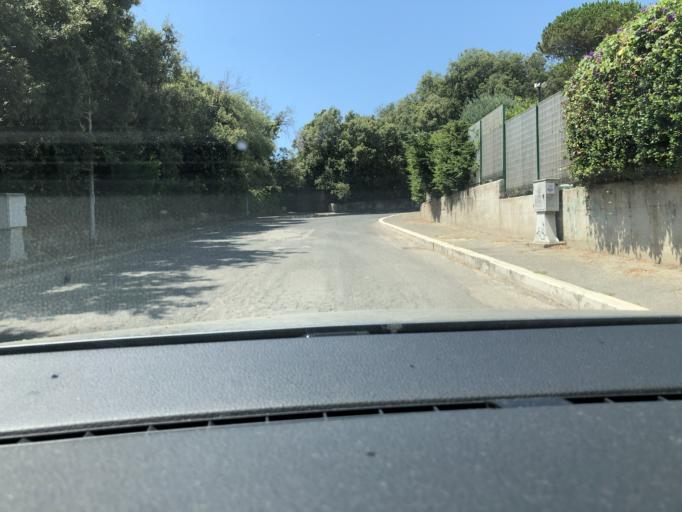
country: IT
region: Latium
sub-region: Citta metropolitana di Roma Capitale
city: Nettuno
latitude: 41.4567
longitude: 12.6483
